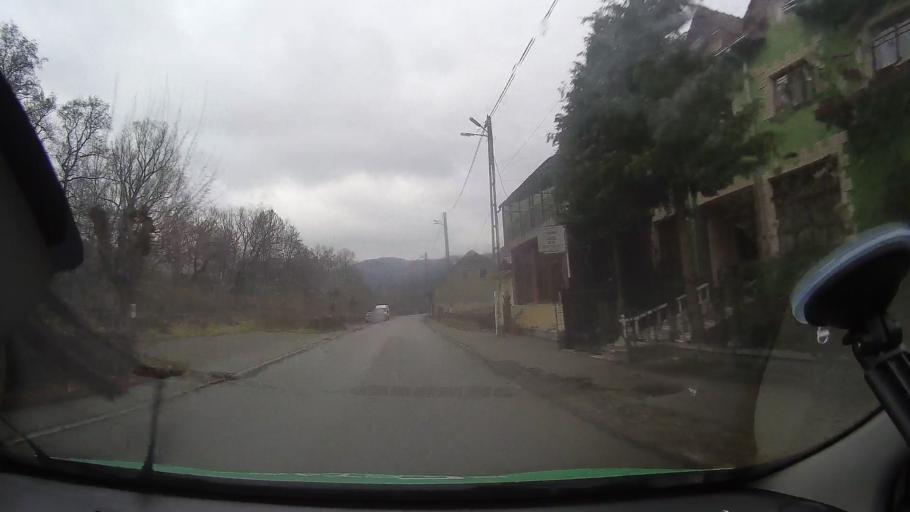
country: RO
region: Hunedoara
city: Vata de Jos
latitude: 46.1802
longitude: 22.6012
